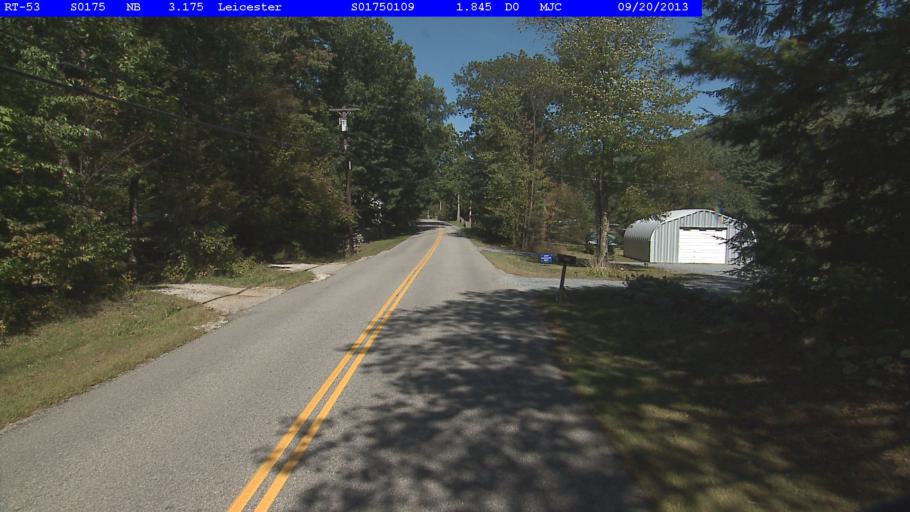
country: US
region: Vermont
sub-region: Rutland County
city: Brandon
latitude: 43.8694
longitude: -73.0650
